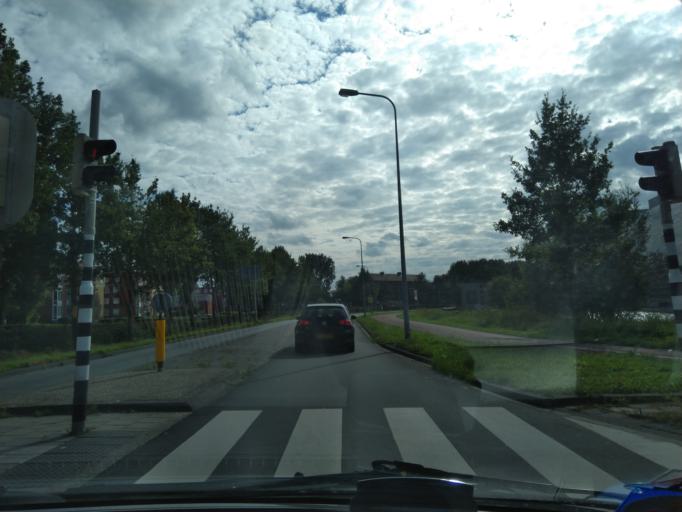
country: NL
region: Groningen
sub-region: Gemeente Groningen
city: Groningen
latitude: 53.1922
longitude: 6.5542
